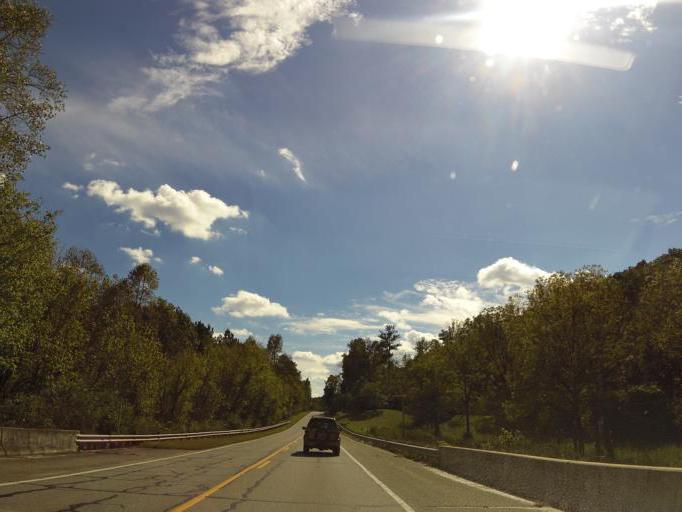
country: US
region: Georgia
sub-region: Pickens County
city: Nelson
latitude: 34.4285
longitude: -84.3662
